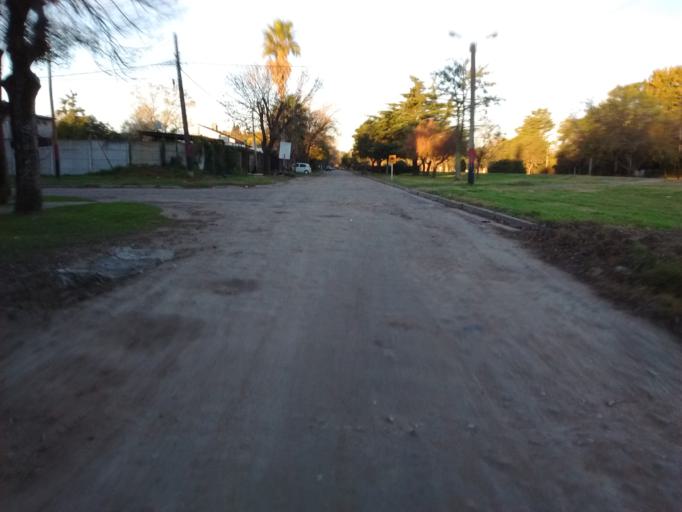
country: AR
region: Santa Fe
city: Funes
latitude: -32.9156
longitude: -60.8175
